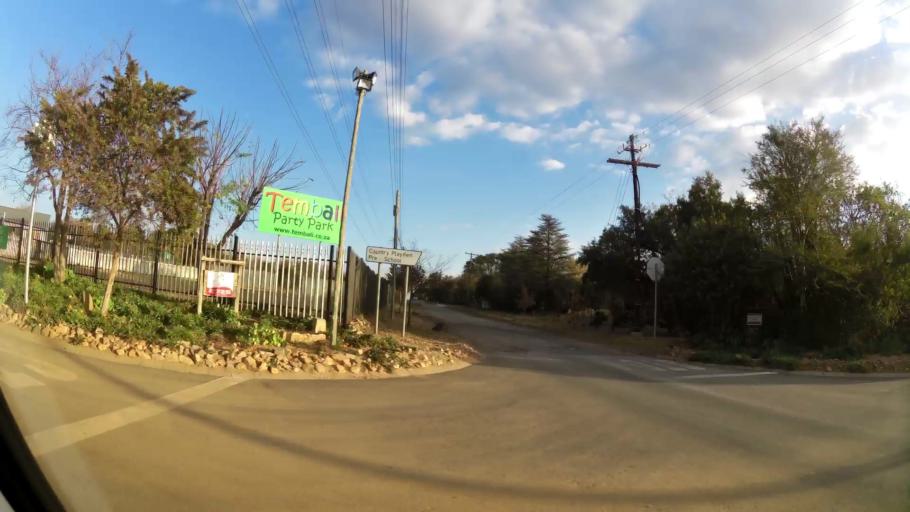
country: ZA
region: Gauteng
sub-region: City of Johannesburg Metropolitan Municipality
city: Diepsloot
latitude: -25.9963
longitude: 27.9782
